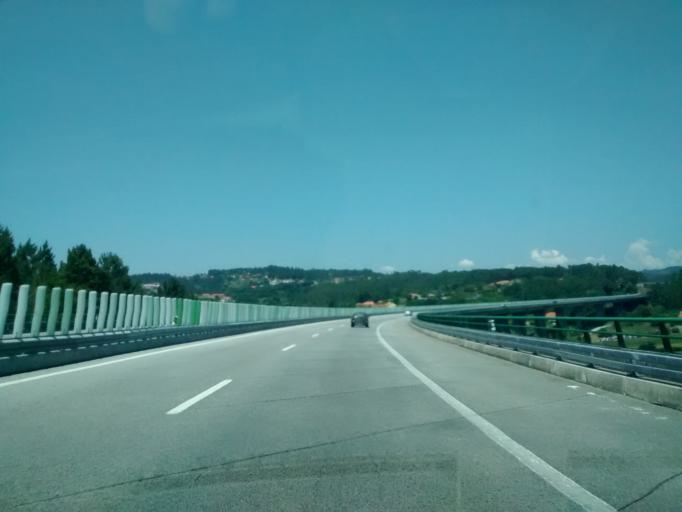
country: PT
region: Viana do Castelo
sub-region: Vila Nova de Cerveira
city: Vila Nova de Cerveira
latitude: 41.8843
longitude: -8.6648
